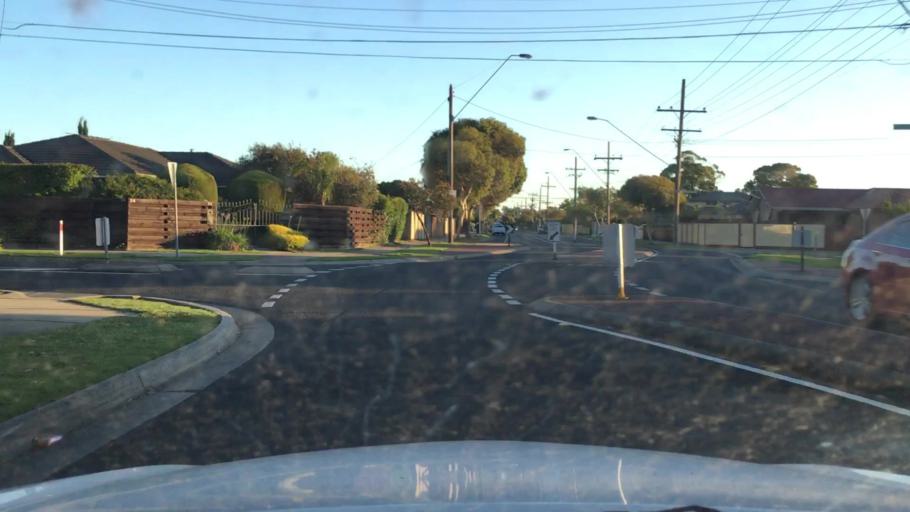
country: AU
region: Victoria
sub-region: Greater Dandenong
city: Keysborough
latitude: -37.9863
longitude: 145.1695
